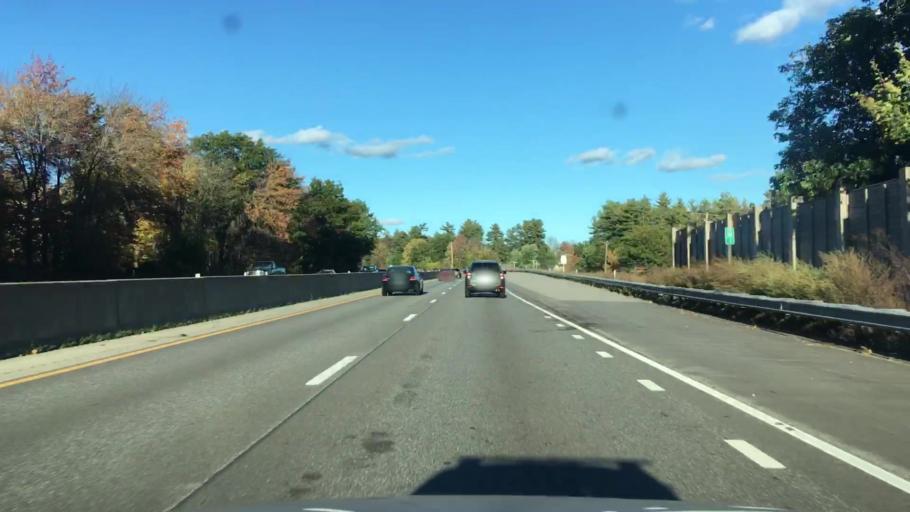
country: US
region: New Hampshire
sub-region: Rockingham County
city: Auburn
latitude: 43.0093
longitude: -71.3874
